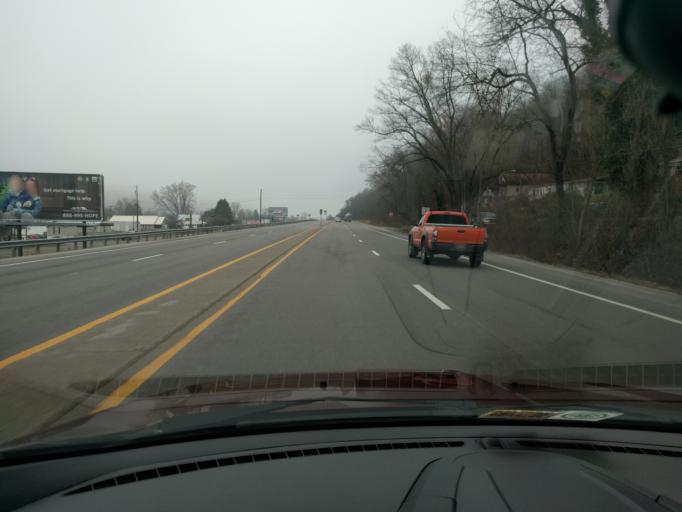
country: US
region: West Virginia
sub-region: Kanawha County
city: Rand
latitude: 38.2726
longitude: -81.5642
